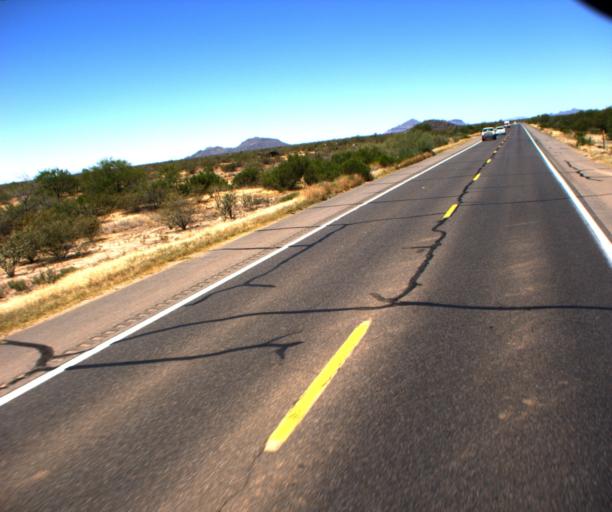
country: US
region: Arizona
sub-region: Yavapai County
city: Congress
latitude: 34.1623
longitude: -113.0064
